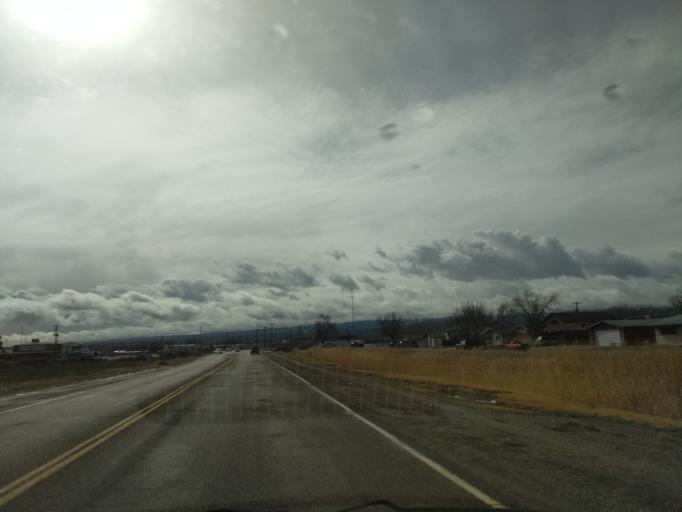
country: US
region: Colorado
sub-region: Mesa County
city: Grand Junction
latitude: 39.0718
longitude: -108.5337
